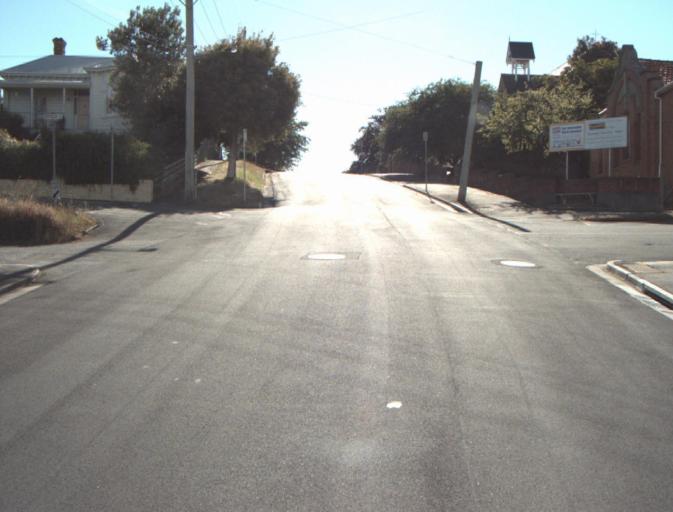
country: AU
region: Tasmania
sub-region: Launceston
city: East Launceston
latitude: -41.4389
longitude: 147.1526
